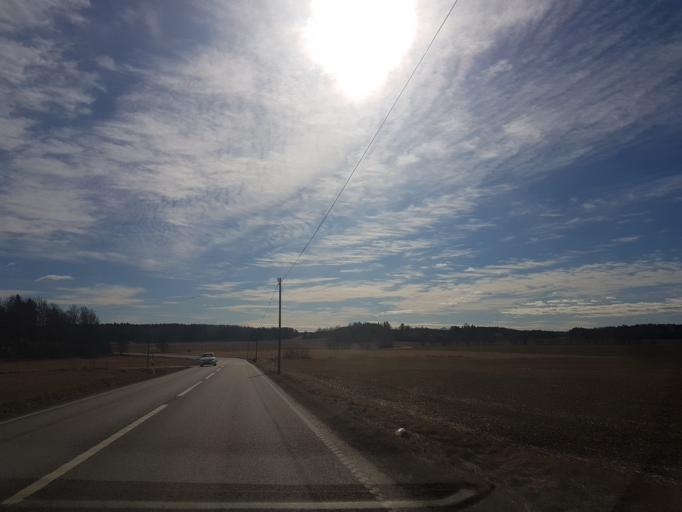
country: SE
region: Stockholm
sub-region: Norrtalje Kommun
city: Rimbo
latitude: 59.7402
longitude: 18.5264
